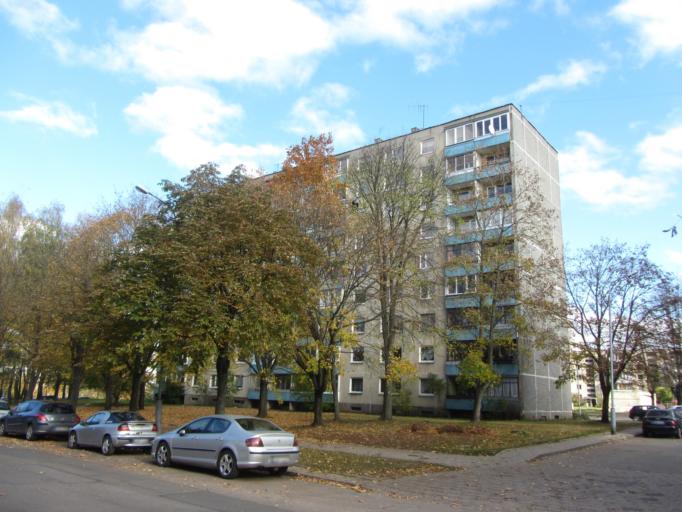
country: LT
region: Vilnius County
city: Lazdynai
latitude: 54.6737
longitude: 25.2097
